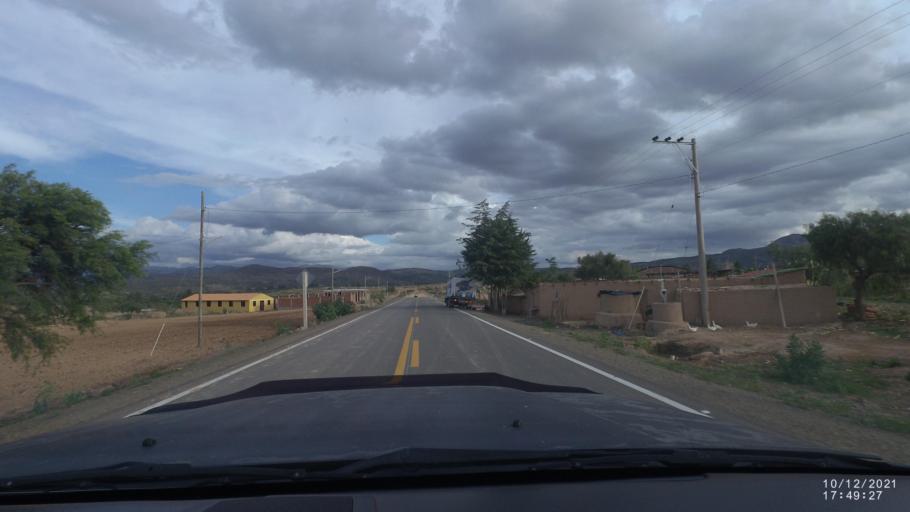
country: BO
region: Cochabamba
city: Tarata
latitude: -17.6566
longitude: -65.9704
